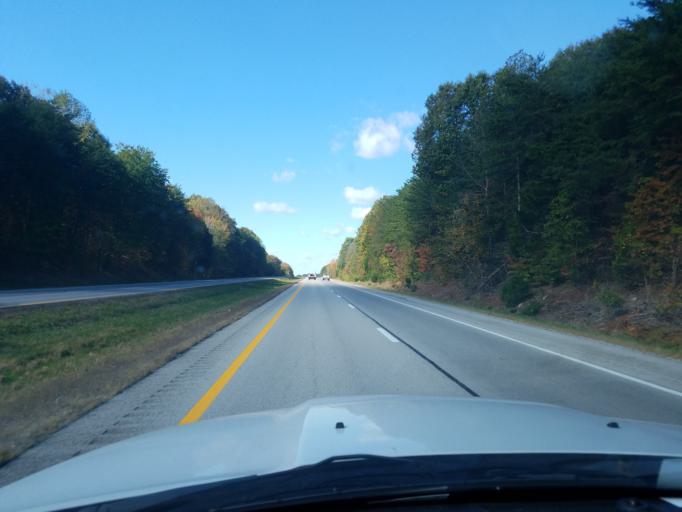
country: US
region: Kentucky
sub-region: Barren County
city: Glasgow
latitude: 36.9972
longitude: -85.8049
